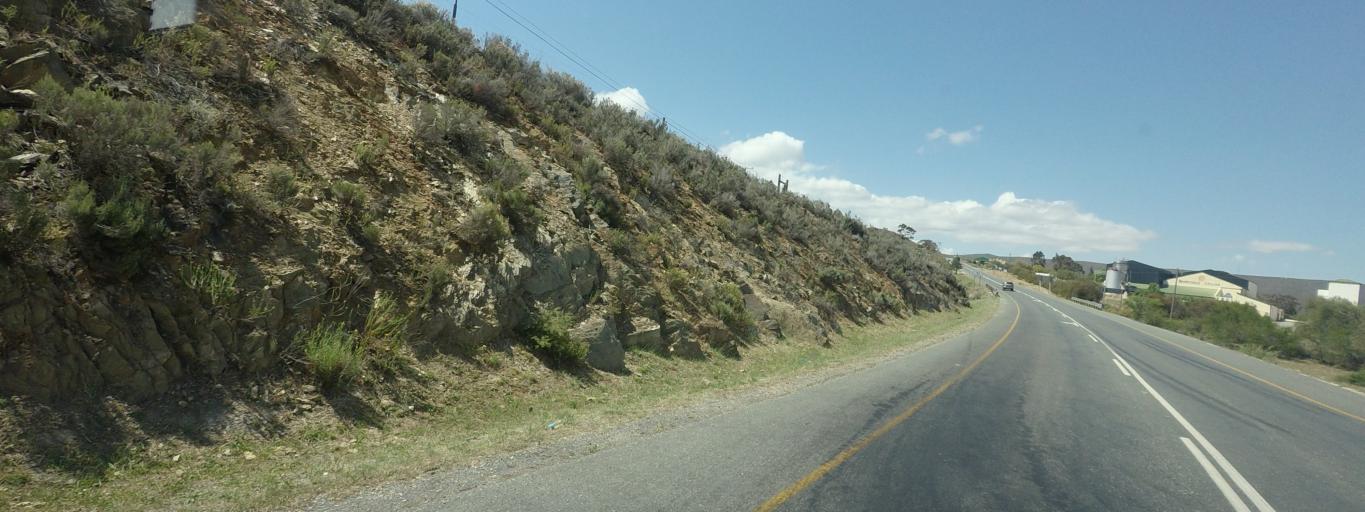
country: ZA
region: Western Cape
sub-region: Overberg District Municipality
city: Swellendam
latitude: -33.9114
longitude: 20.7099
